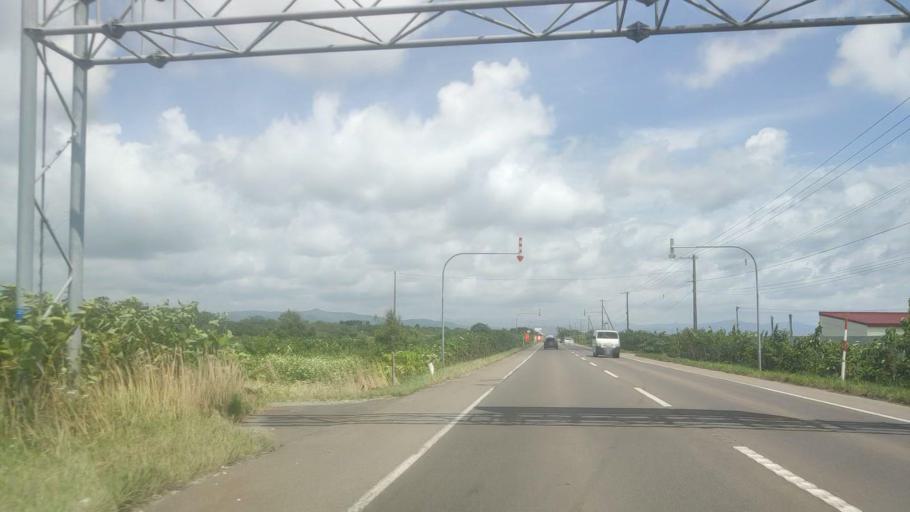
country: JP
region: Hokkaido
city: Niseko Town
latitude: 42.4851
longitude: 140.3535
